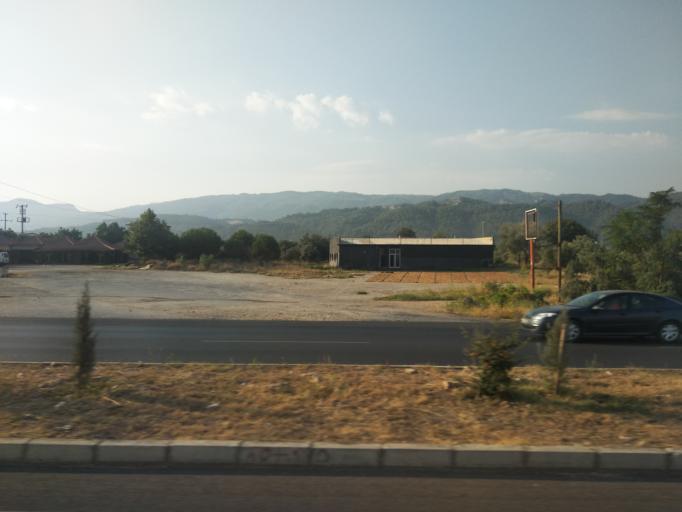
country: TR
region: Manisa
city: Ahmetli
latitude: 38.5048
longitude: 27.8821
